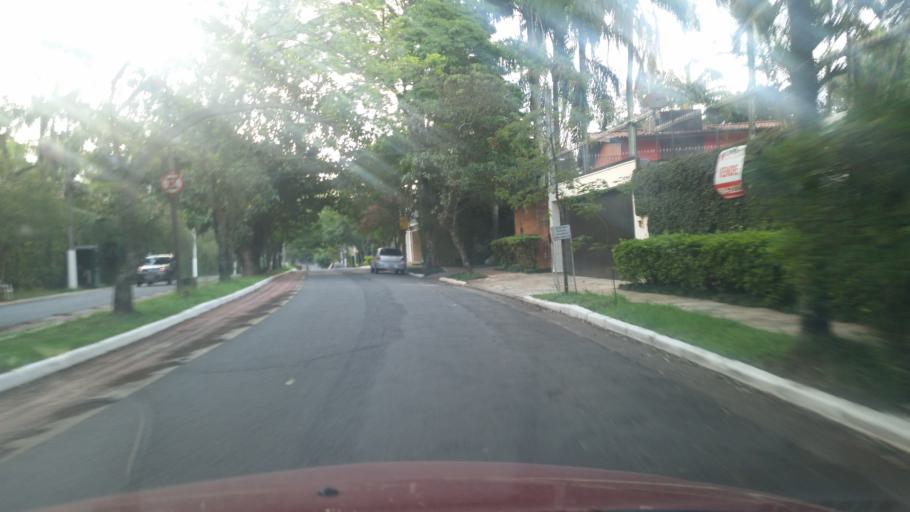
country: BR
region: Sao Paulo
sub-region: Diadema
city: Diadema
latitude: -23.6364
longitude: -46.6840
